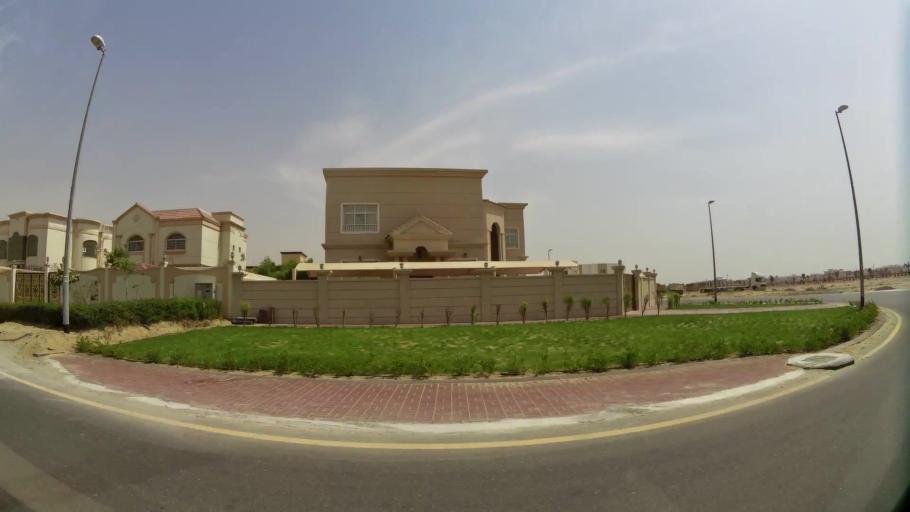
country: AE
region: Ash Shariqah
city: Sharjah
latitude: 25.2649
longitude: 55.4775
